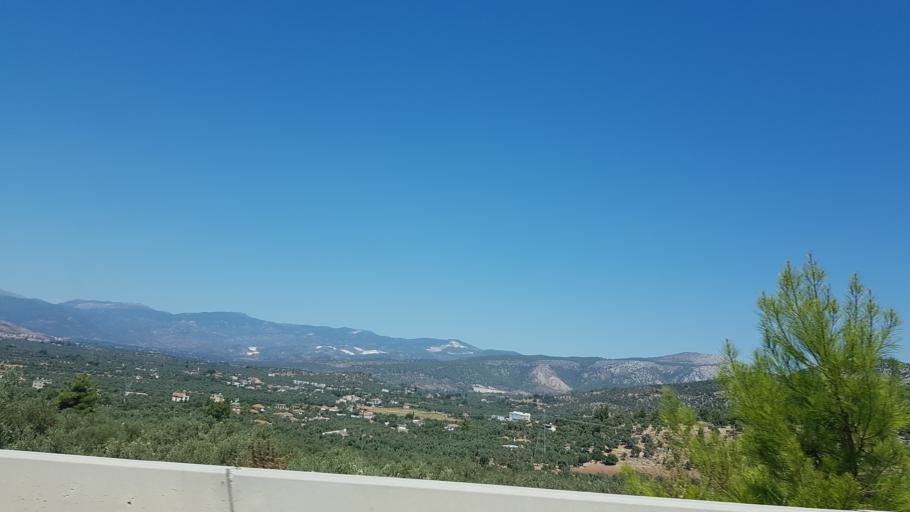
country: TR
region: Mugla
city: Milas
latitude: 37.2854
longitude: 27.8202
